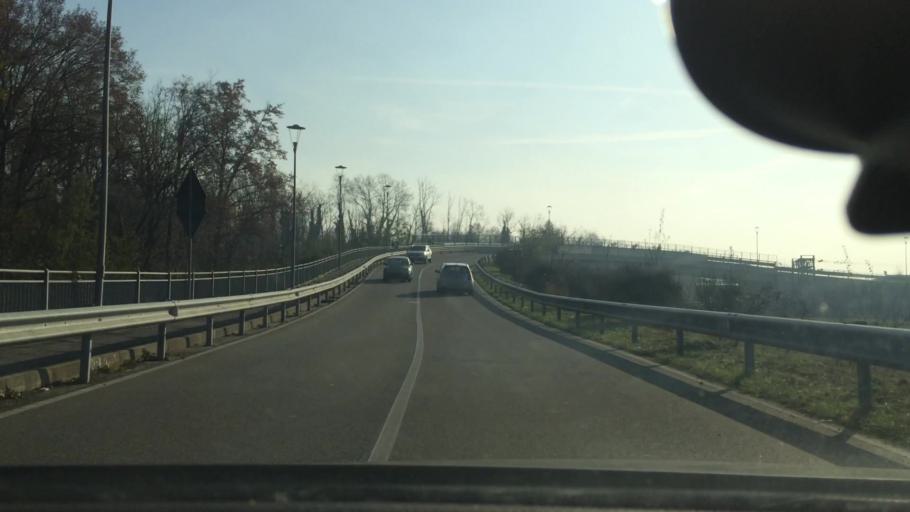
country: IT
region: Lombardy
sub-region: Provincia di Monza e Brianza
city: Ceriano Laghetto
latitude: 45.6270
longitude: 9.0865
